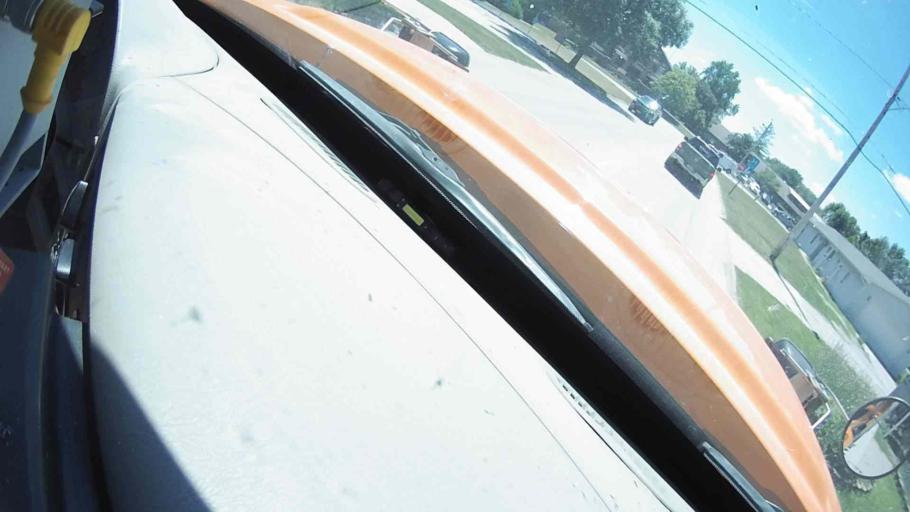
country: US
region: Iowa
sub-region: Washington County
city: Washington
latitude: 41.2991
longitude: -91.6786
